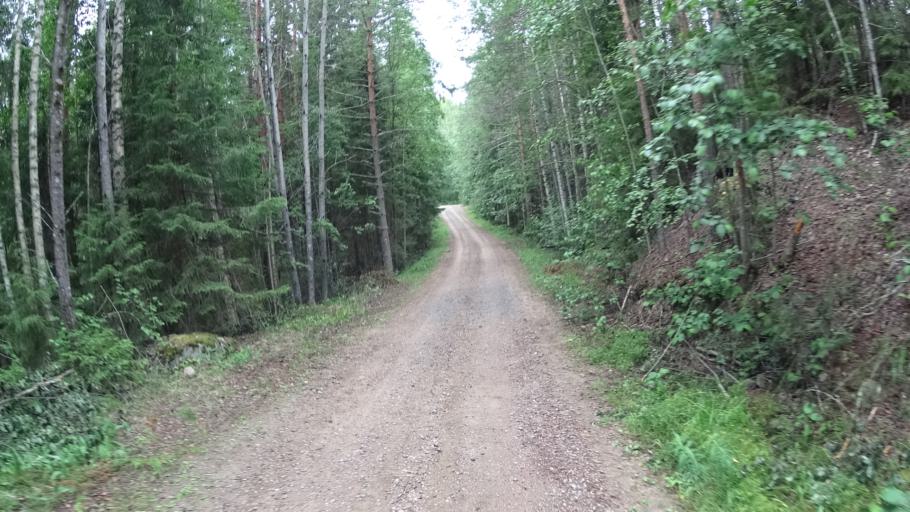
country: FI
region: Southern Savonia
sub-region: Mikkeli
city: Maentyharju
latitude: 61.1832
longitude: 26.8333
